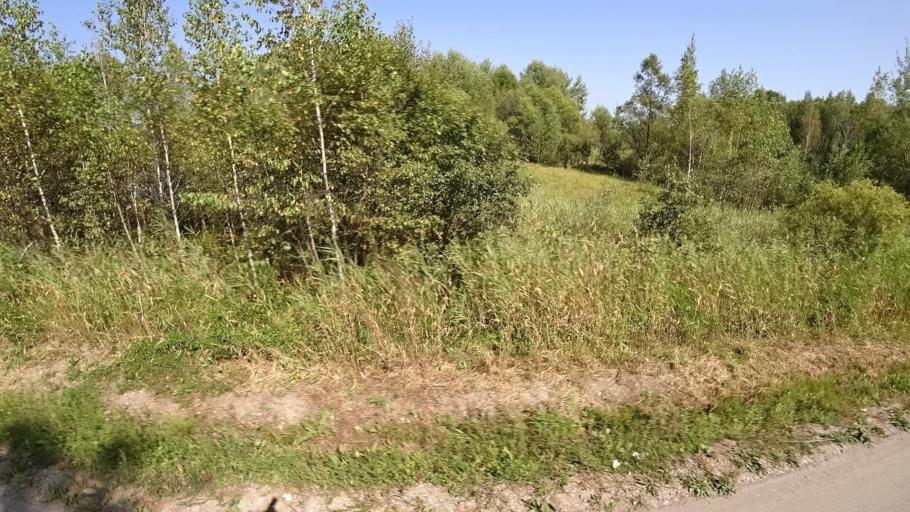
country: RU
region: Khabarovsk Krai
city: Khor
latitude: 47.9753
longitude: 135.1130
